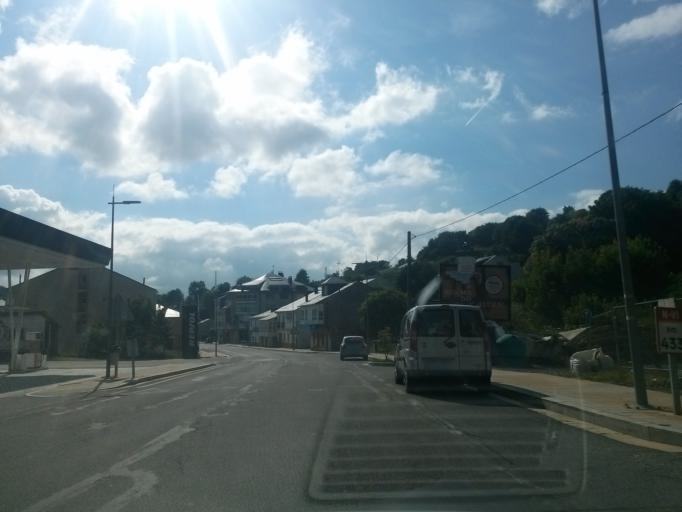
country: ES
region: Castille and Leon
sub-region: Provincia de Leon
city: Balboa
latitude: 42.7267
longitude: -7.0220
